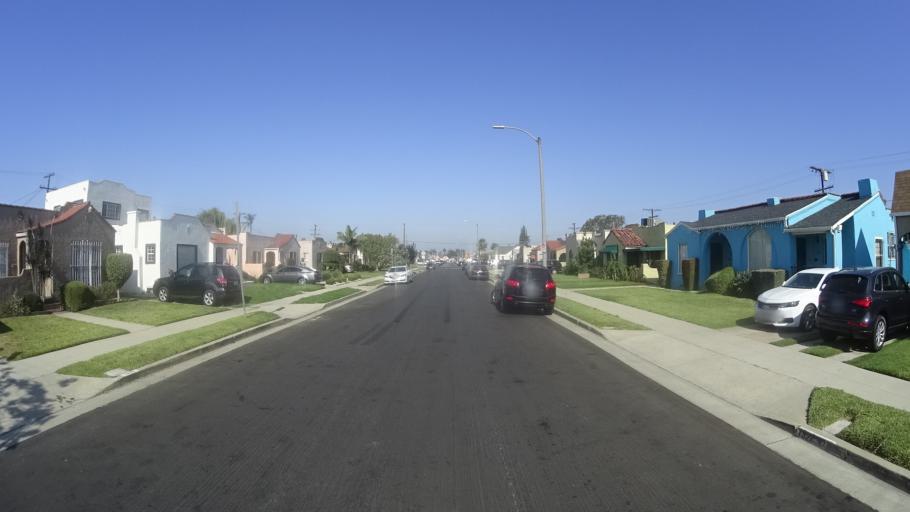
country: US
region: California
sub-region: Los Angeles County
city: Westmont
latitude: 33.9785
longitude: -118.3122
